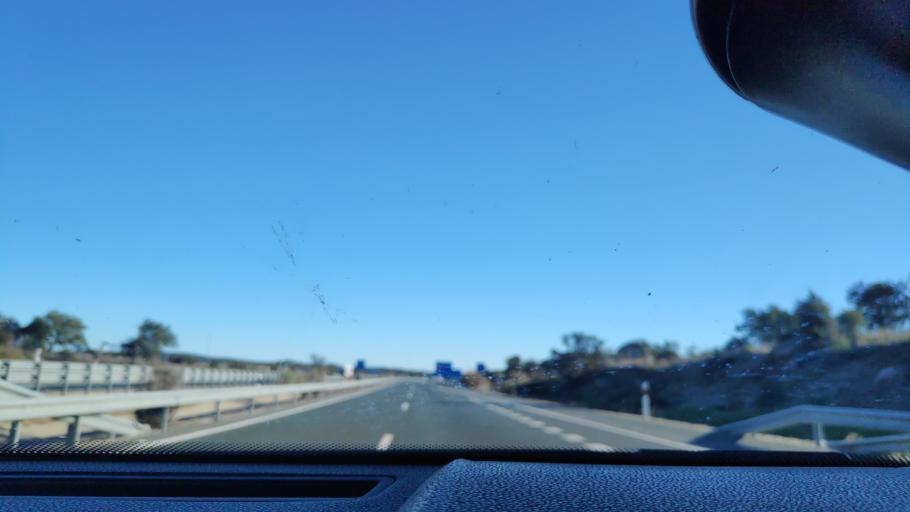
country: ES
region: Andalusia
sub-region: Provincia de Huelva
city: Santa Olalla del Cala
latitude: 37.9161
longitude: -6.2212
